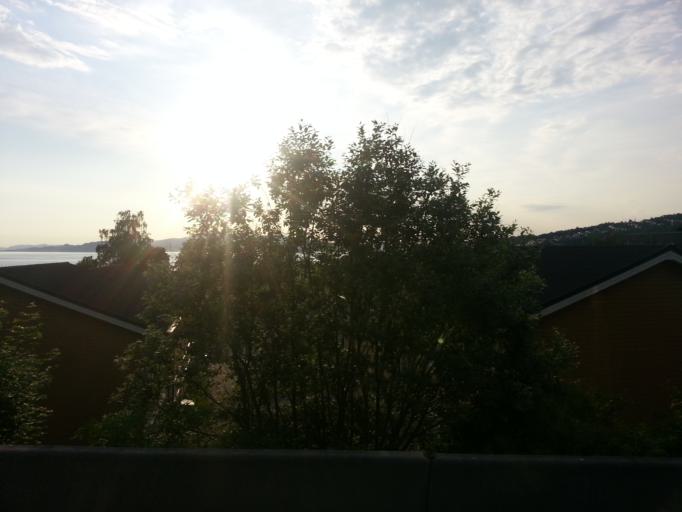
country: NO
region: Sor-Trondelag
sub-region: Malvik
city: Malvik
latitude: 63.4381
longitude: 10.6028
